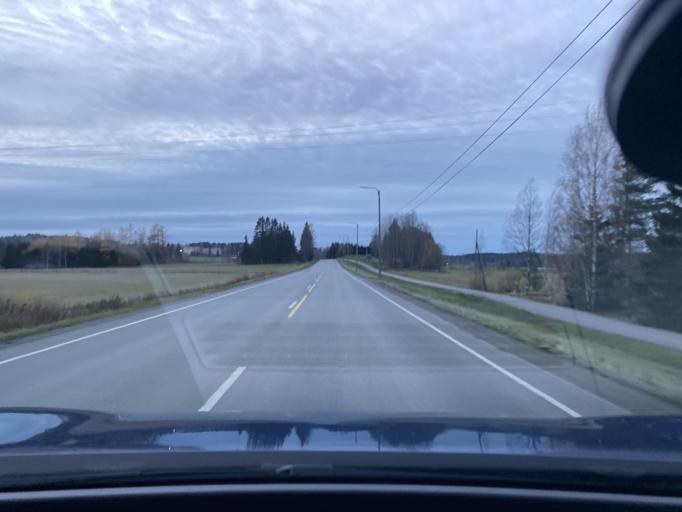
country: FI
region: Uusimaa
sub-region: Helsinki
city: Saukkola
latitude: 60.3844
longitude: 23.9325
